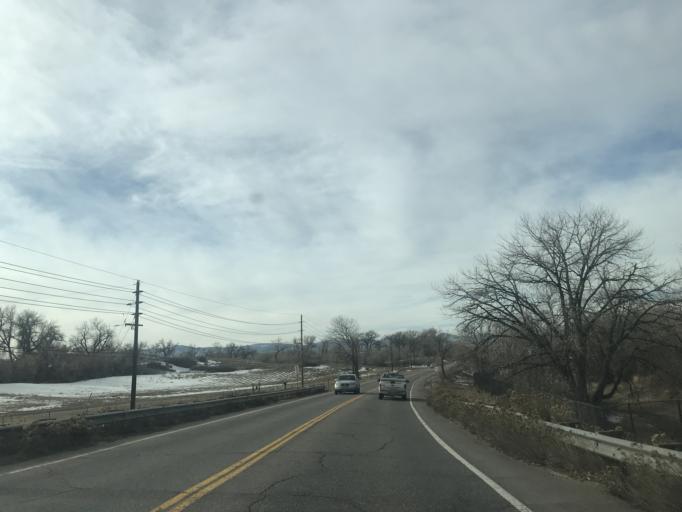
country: US
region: Colorado
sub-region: Douglas County
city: Highlands Ranch
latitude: 39.5645
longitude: -105.0005
